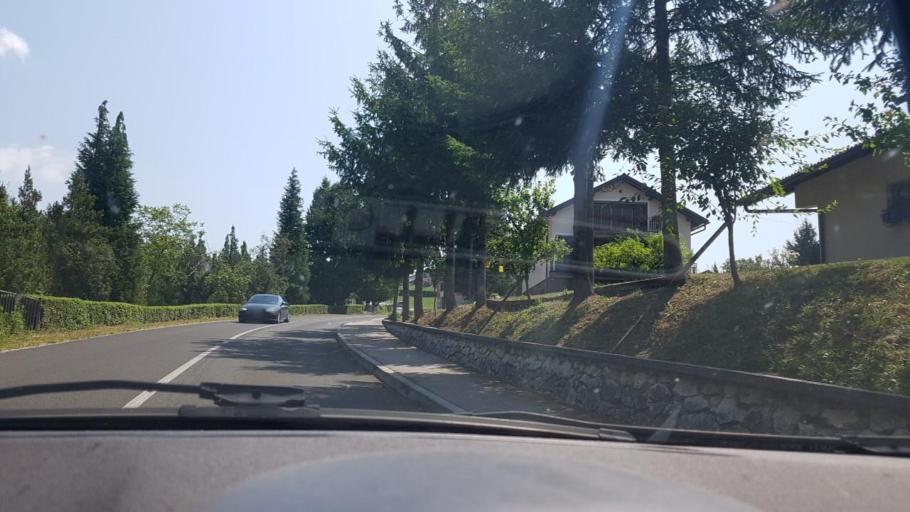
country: SI
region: Rogatec
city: Rogatec
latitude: 46.2140
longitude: 15.6679
